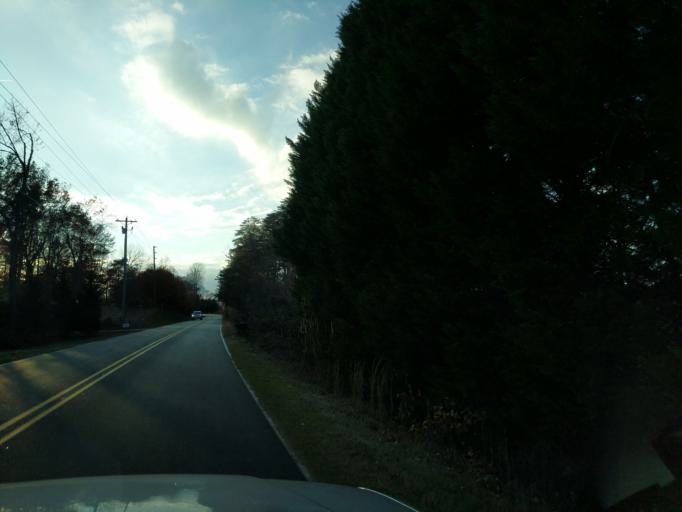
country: US
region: North Carolina
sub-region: Polk County
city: Columbus
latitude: 35.2571
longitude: -82.0731
